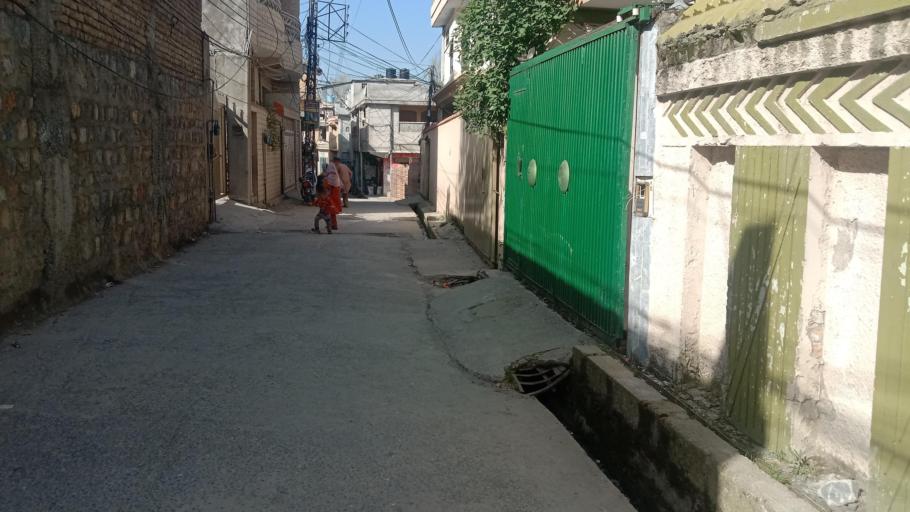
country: PK
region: Khyber Pakhtunkhwa
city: Abbottabad
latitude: 34.1769
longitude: 73.2251
